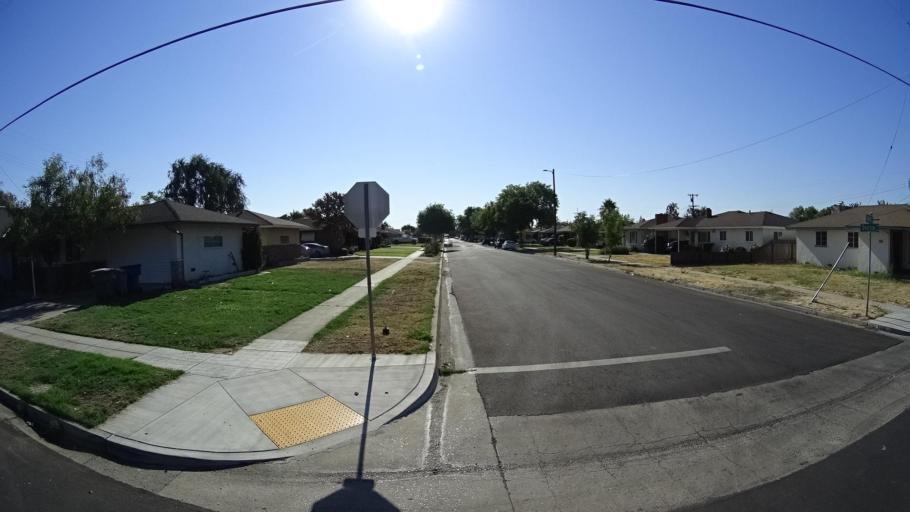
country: US
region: California
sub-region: Fresno County
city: Fresno
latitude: 36.7831
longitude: -119.7589
